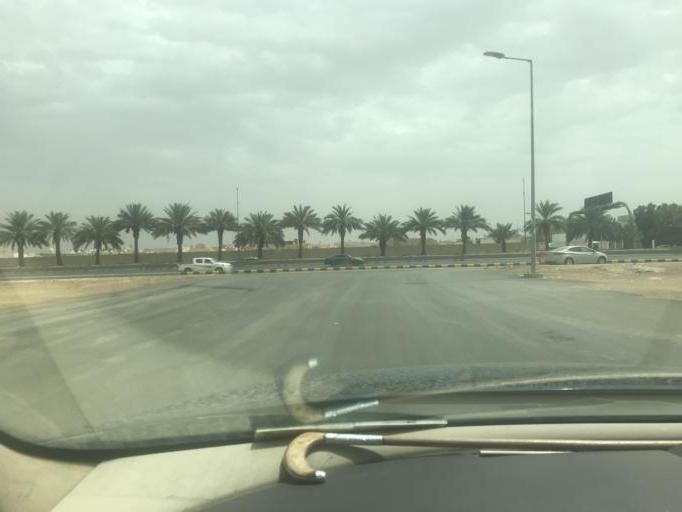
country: SA
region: Ar Riyad
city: Riyadh
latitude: 24.7902
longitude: 46.7146
